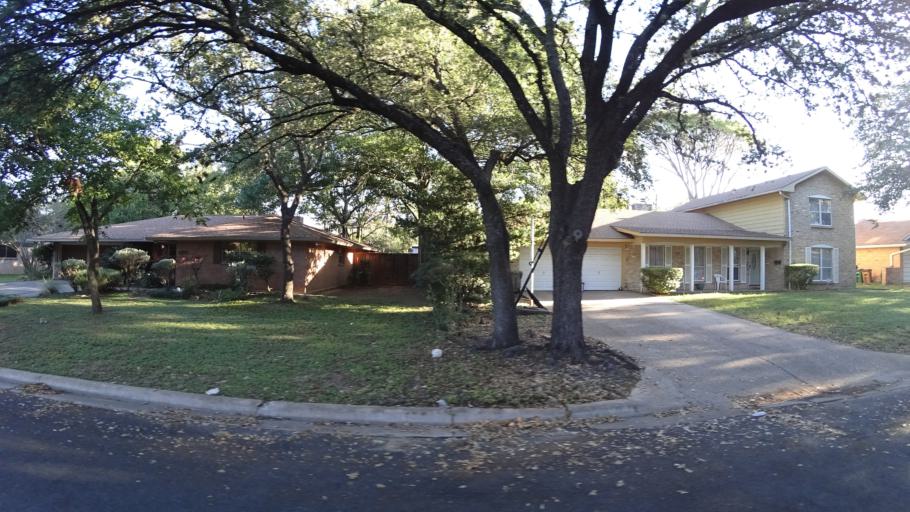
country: US
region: Texas
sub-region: Travis County
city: Austin
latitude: 30.3076
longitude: -97.6838
